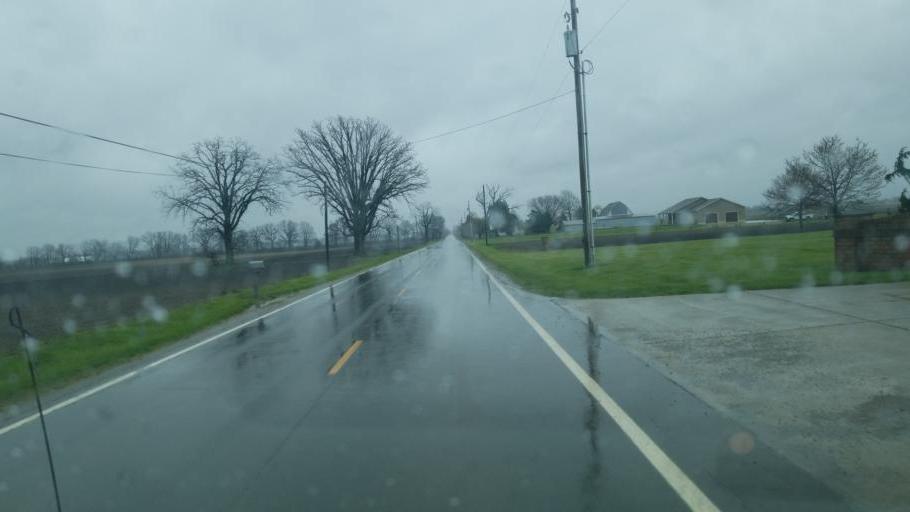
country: US
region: Ohio
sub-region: Wyandot County
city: Upper Sandusky
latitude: 40.8179
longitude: -83.3197
